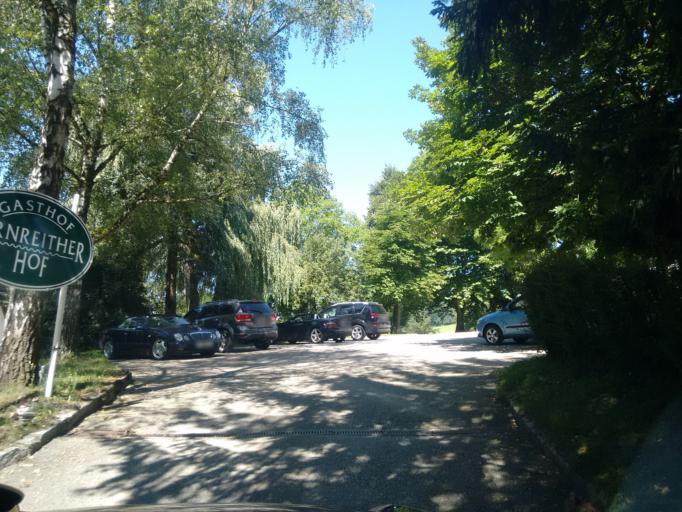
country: AT
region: Upper Austria
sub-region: Wels-Land
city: Gunskirchen
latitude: 48.1751
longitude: 13.9470
